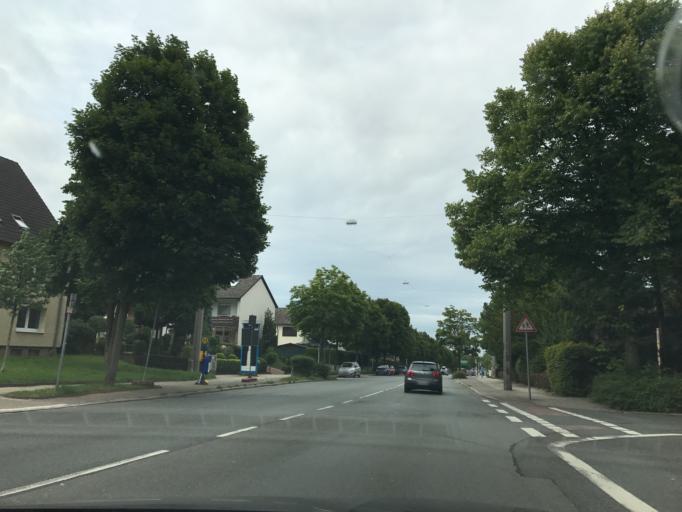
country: DE
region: North Rhine-Westphalia
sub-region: Regierungsbezirk Munster
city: Bottrop
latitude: 51.4824
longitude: 6.9487
